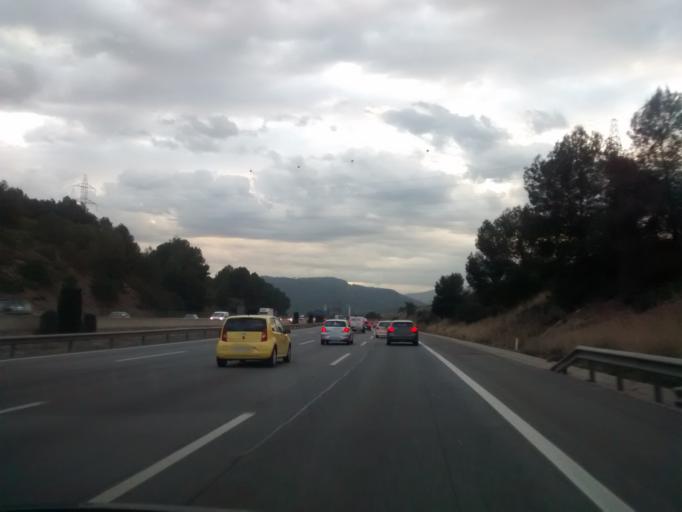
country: ES
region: Catalonia
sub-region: Provincia de Barcelona
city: Castellbisbal
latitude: 41.4604
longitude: 2.0102
